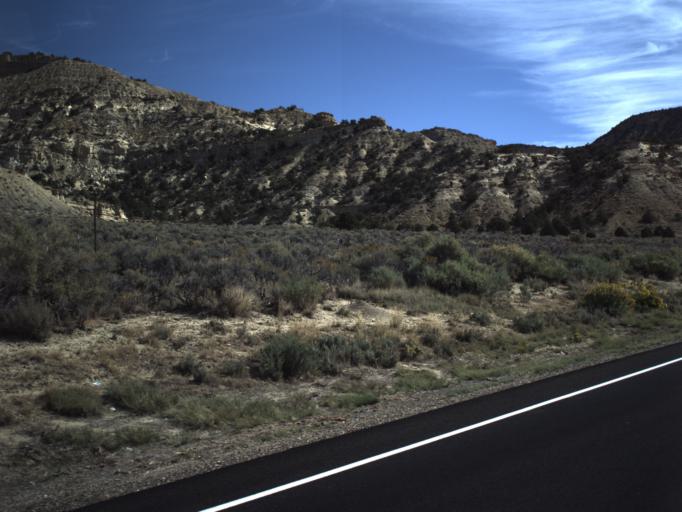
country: US
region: Utah
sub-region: Garfield County
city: Panguitch
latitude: 37.5930
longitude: -111.9350
